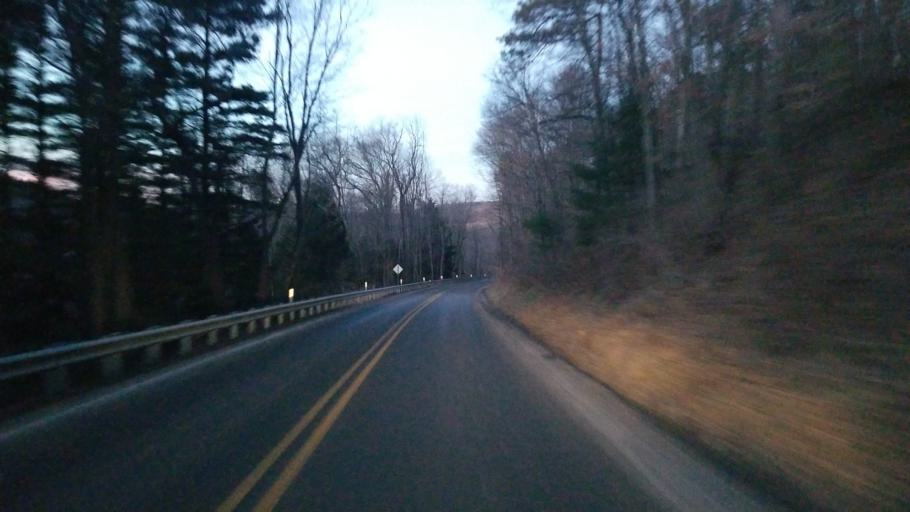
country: US
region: Pennsylvania
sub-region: Jefferson County
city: Punxsutawney
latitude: 40.8630
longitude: -79.1726
